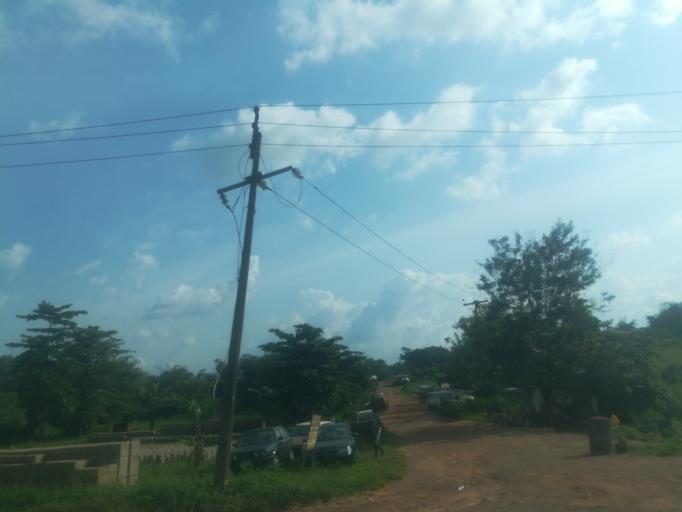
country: NG
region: Oyo
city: Ido
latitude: 7.3964
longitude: 3.7907
